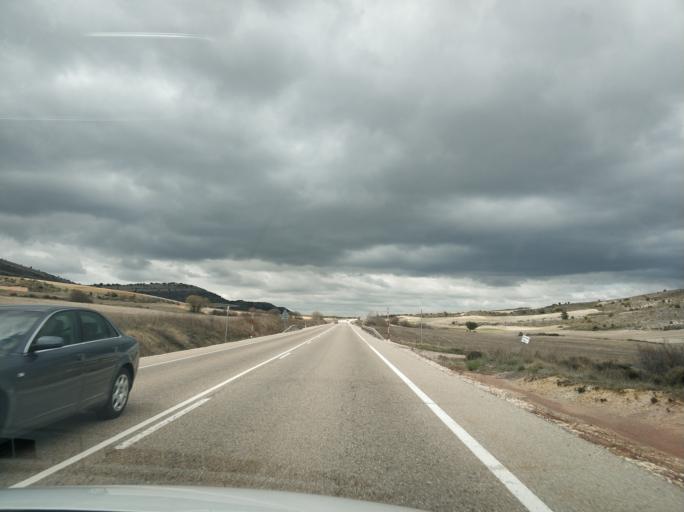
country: ES
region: Castille and Leon
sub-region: Provincia de Burgos
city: Covarrubias
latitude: 42.1075
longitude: -3.5141
